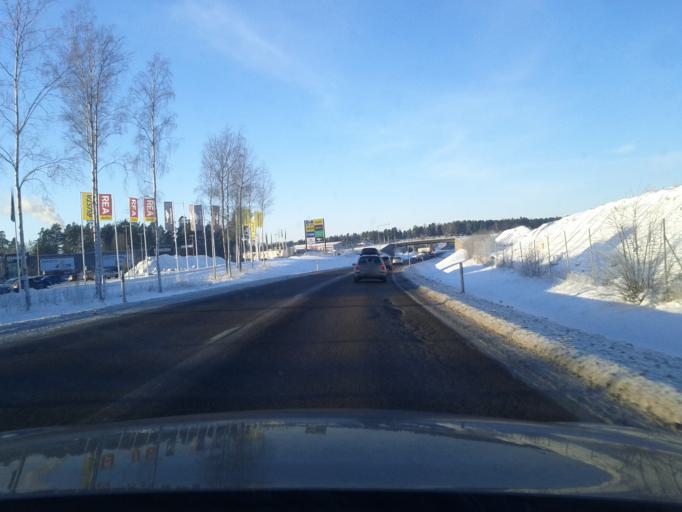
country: SE
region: Dalarna
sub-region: Faluns Kommun
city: Falun
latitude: 60.6057
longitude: 15.6674
